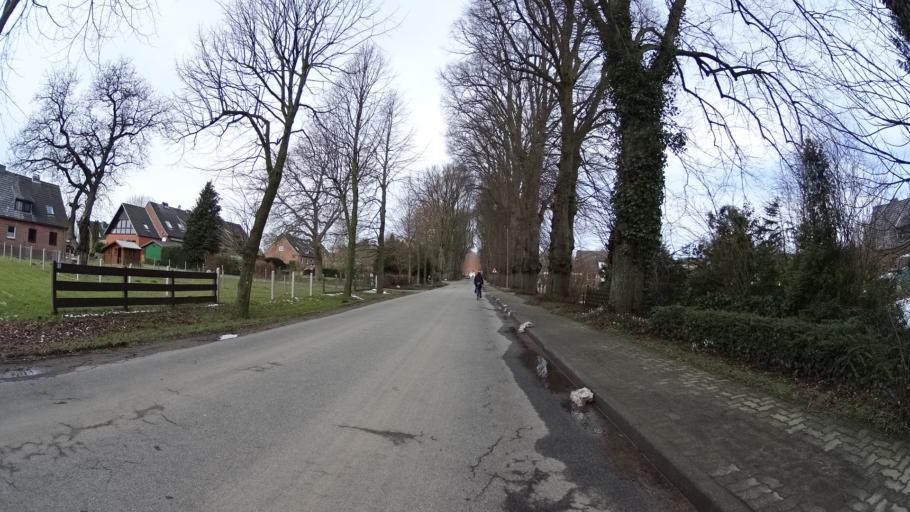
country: DE
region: Schleswig-Holstein
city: Rendswuhren
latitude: 54.0806
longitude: 10.1961
